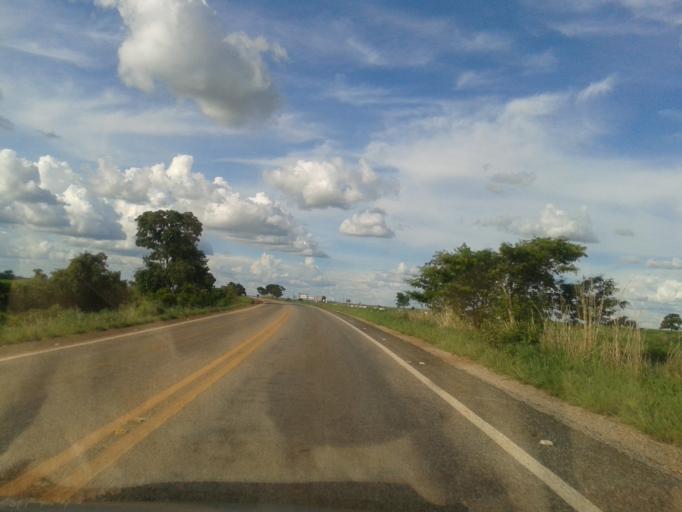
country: BR
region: Goias
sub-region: Mozarlandia
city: Mozarlandia
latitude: -14.5306
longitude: -50.4861
